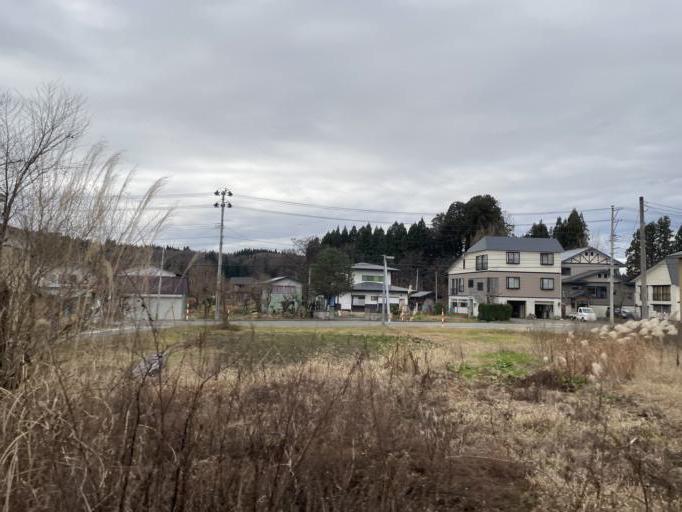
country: JP
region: Yamagata
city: Shinjo
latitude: 38.8648
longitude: 140.2592
